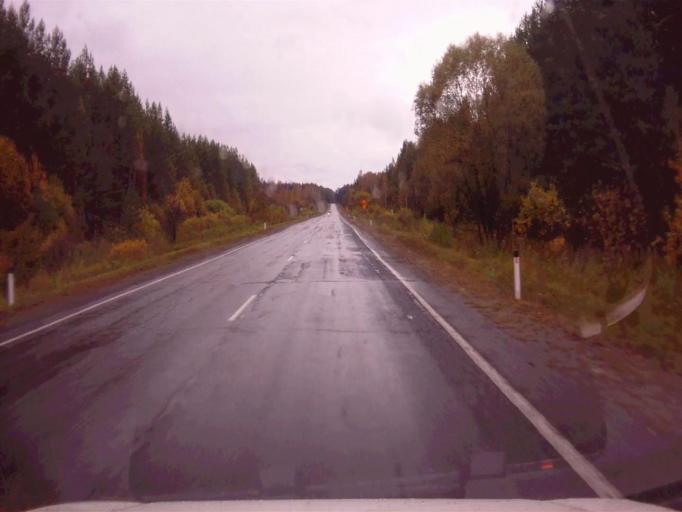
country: RU
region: Chelyabinsk
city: Verkhniy Ufaley
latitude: 56.0152
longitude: 60.3106
